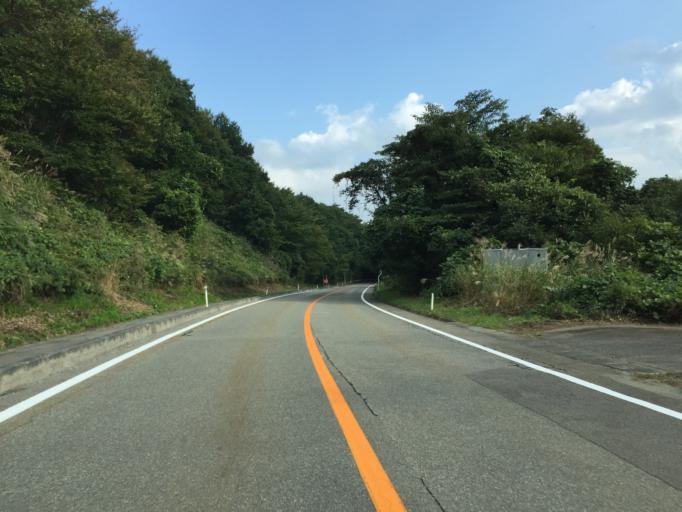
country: JP
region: Fukushima
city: Funehikimachi-funehiki
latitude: 37.5721
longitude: 140.7350
